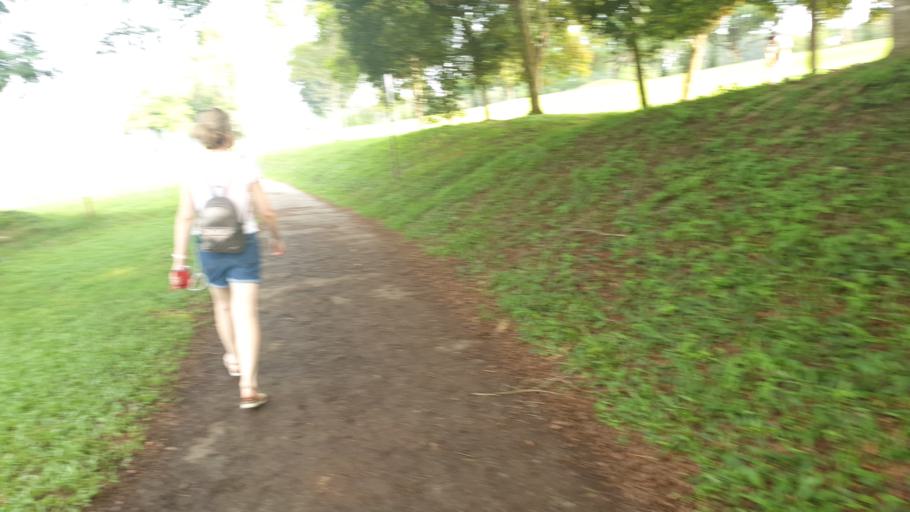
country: SG
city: Singapore
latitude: 1.3443
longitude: 103.8134
